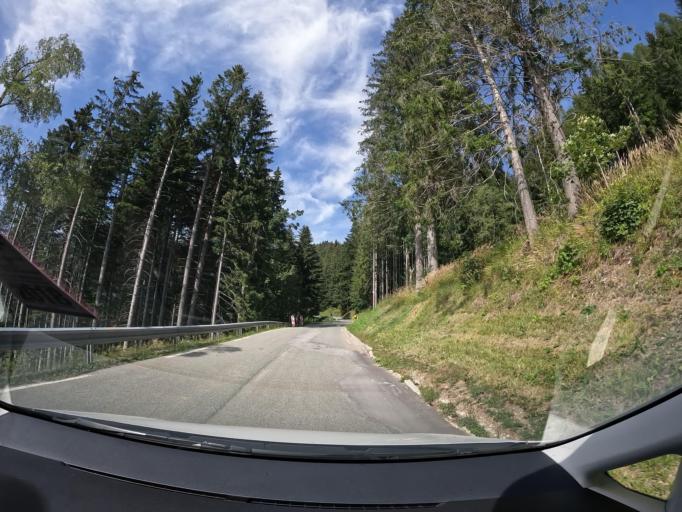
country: AT
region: Carinthia
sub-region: Politischer Bezirk Klagenfurt Land
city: Maria Saal
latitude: 46.6954
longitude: 14.3165
